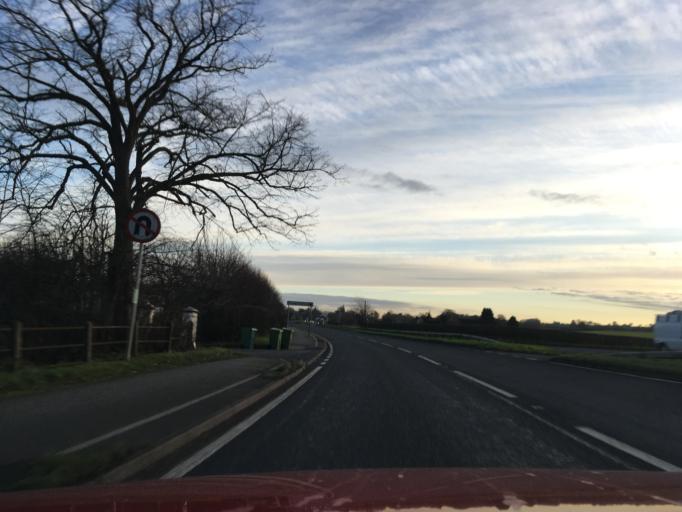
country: GB
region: England
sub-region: Staffordshire
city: Stone
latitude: 52.8809
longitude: -2.1333
